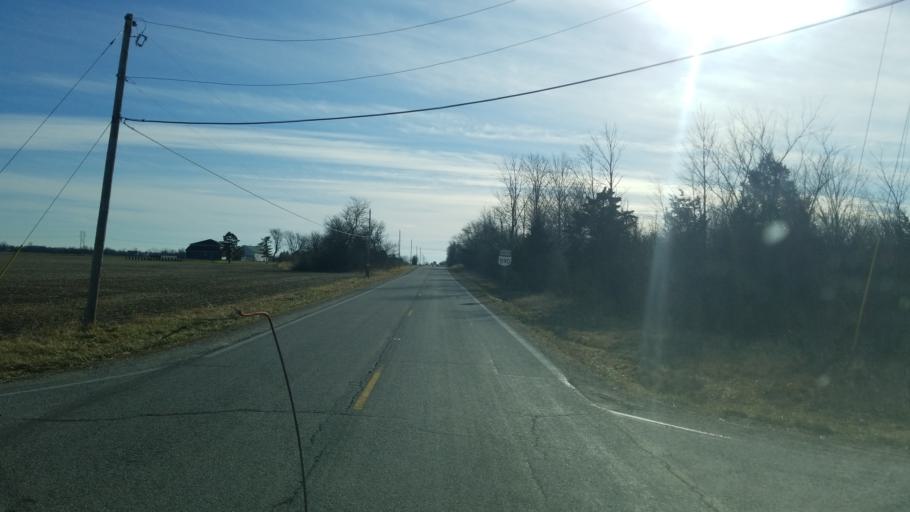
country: US
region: Ohio
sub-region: Sandusky County
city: Stony Prairie
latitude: 41.3633
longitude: -83.2230
